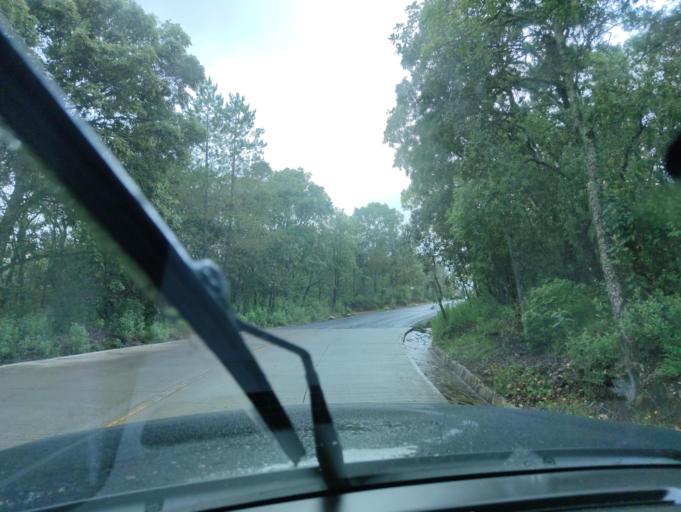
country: MX
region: Mexico
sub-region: Morelos
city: San Marcos Tlazalpan
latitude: 19.8741
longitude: -99.6610
